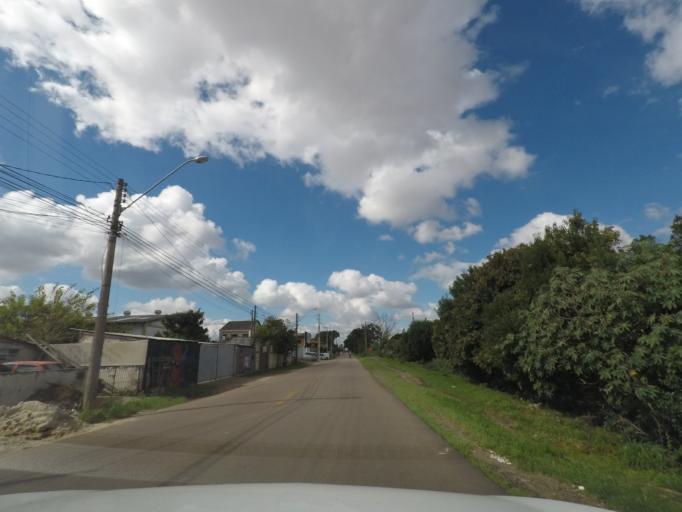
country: BR
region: Parana
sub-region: Curitiba
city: Curitiba
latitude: -25.4734
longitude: -49.2443
